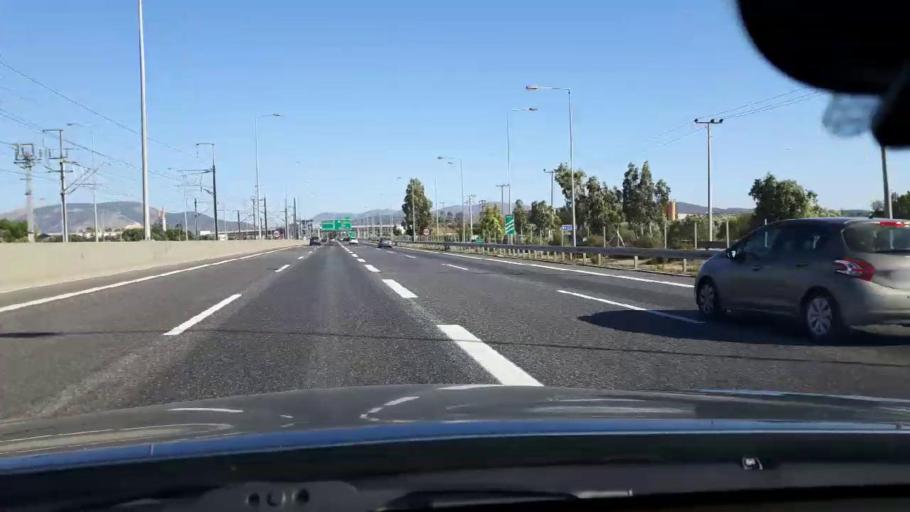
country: GR
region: Attica
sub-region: Nomarchia Anatolikis Attikis
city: Koropi
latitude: 37.9071
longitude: 23.9003
